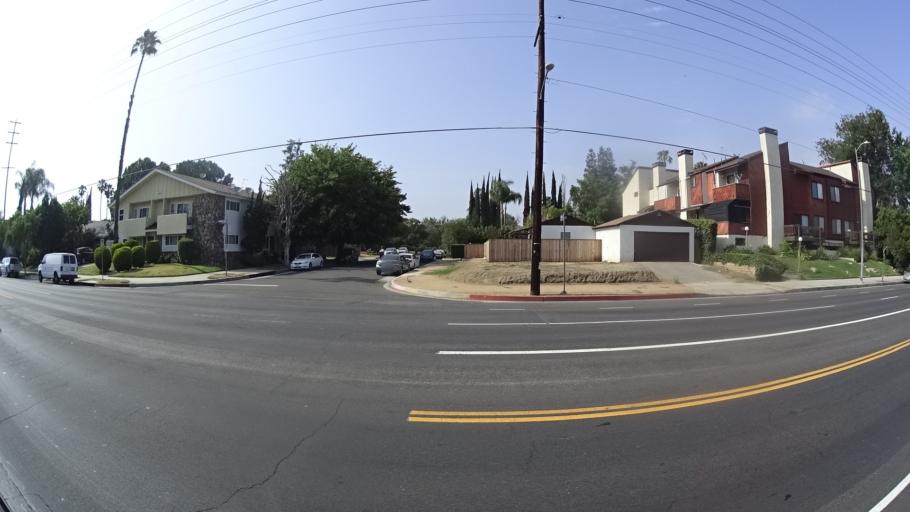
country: US
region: California
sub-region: Los Angeles County
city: Van Nuys
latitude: 34.1722
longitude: -118.4345
